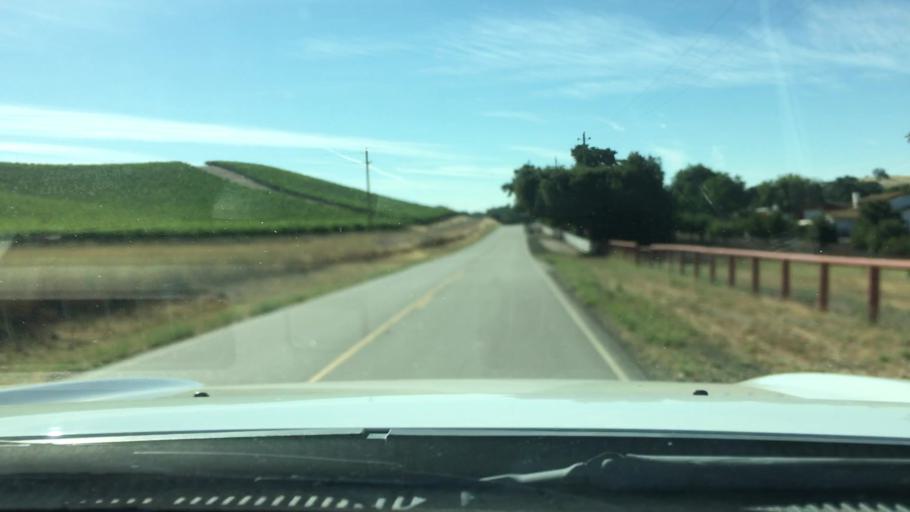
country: US
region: California
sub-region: San Luis Obispo County
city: Templeton
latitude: 35.5584
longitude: -120.6312
